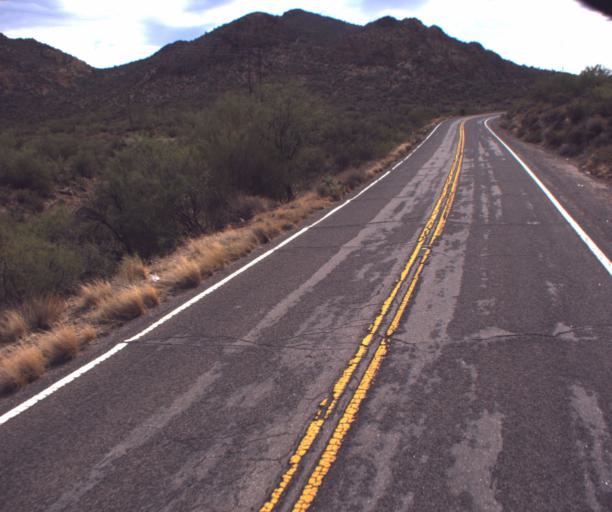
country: US
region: Arizona
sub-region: Pinal County
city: Apache Junction
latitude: 33.5155
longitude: -111.4574
